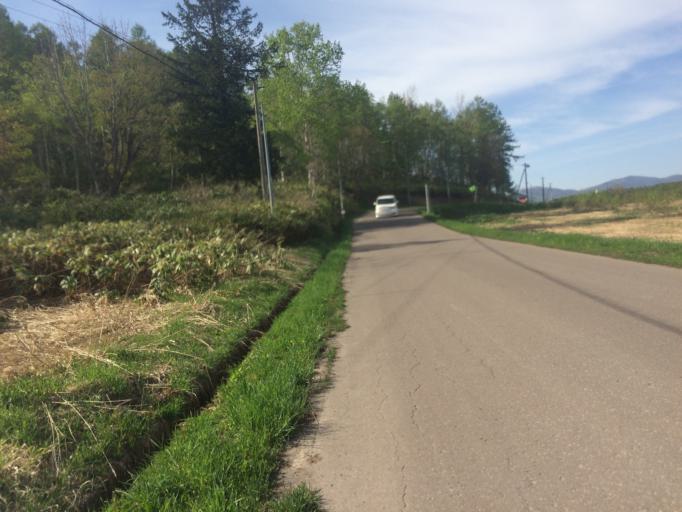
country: JP
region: Hokkaido
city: Niseko Town
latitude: 42.9060
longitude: 140.7399
